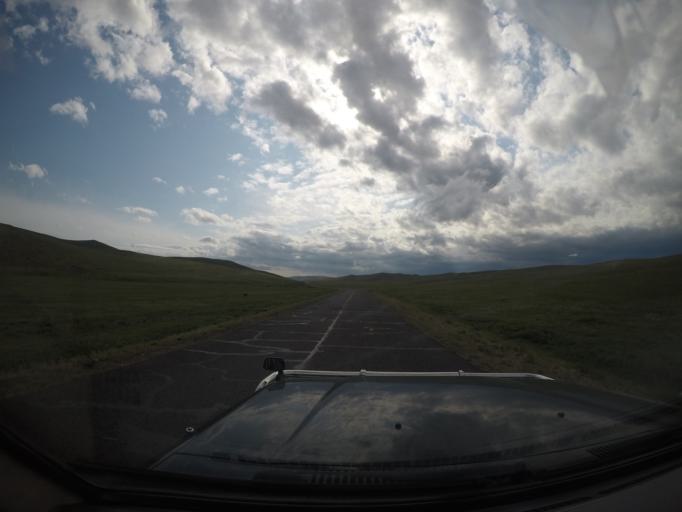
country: MN
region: Hentiy
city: Modot
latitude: 47.7961
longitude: 108.6908
